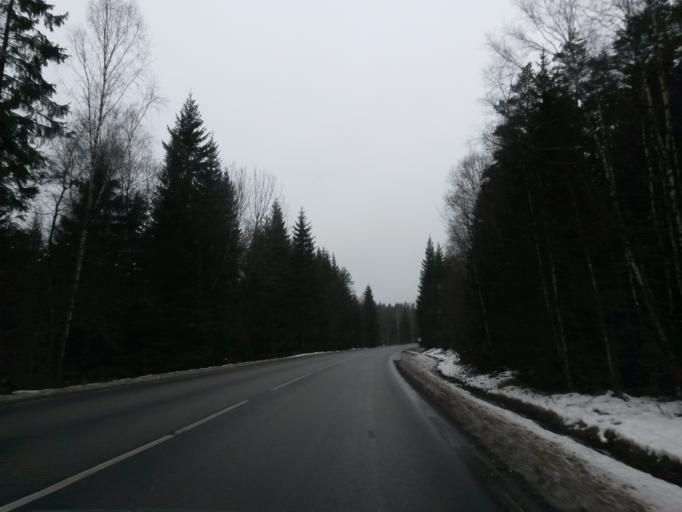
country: SE
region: Vaestra Goetaland
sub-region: Tranemo Kommun
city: Langhem
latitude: 57.6910
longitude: 13.2116
